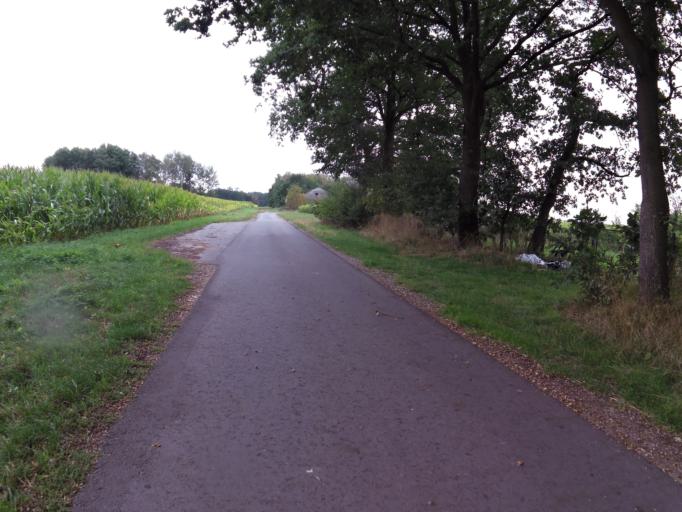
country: DE
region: Lower Saxony
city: Scheessel
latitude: 53.1569
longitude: 9.4557
